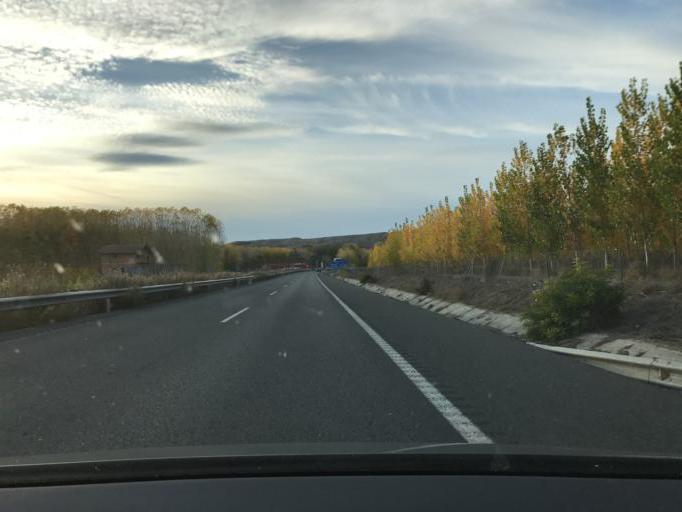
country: ES
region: Andalusia
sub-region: Provincia de Granada
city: Purullena
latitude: 37.3284
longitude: -3.2123
